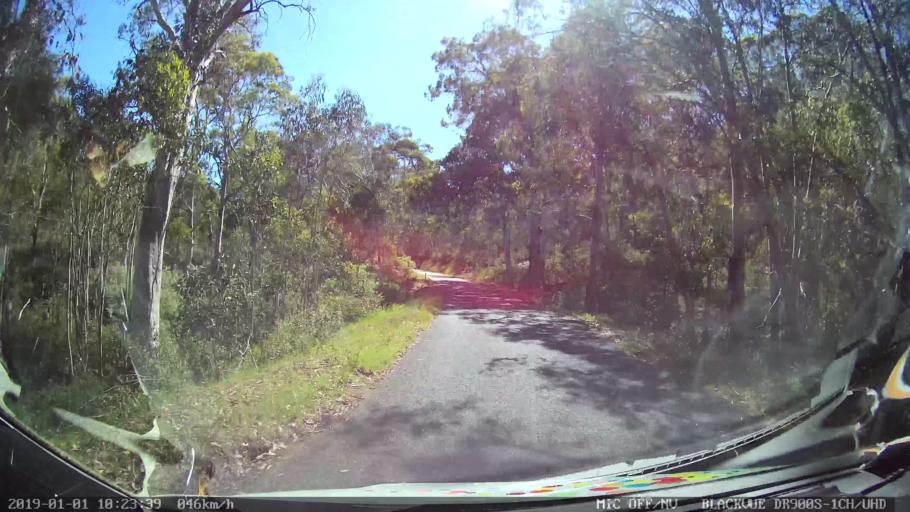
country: AU
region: New South Wales
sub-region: Snowy River
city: Jindabyne
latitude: -36.0752
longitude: 148.2135
